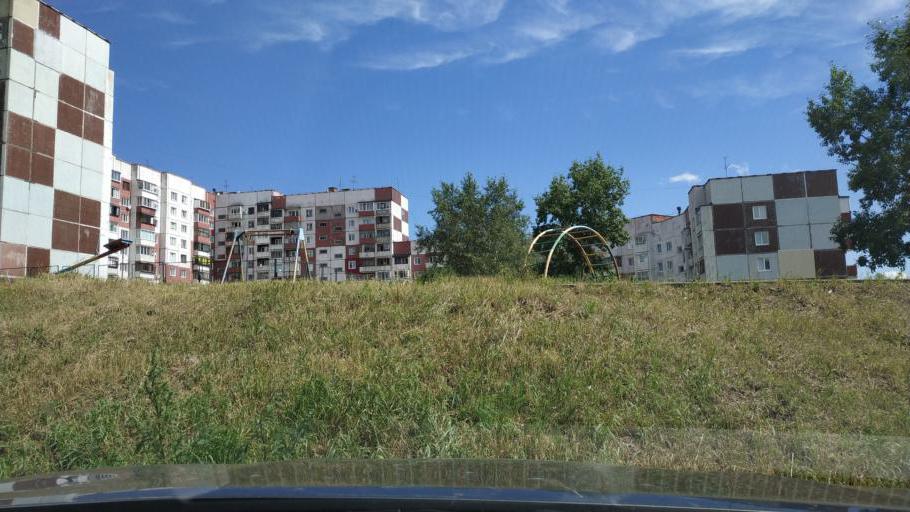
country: RU
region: Irkutsk
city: Bratsk
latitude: 56.1470
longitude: 101.6380
